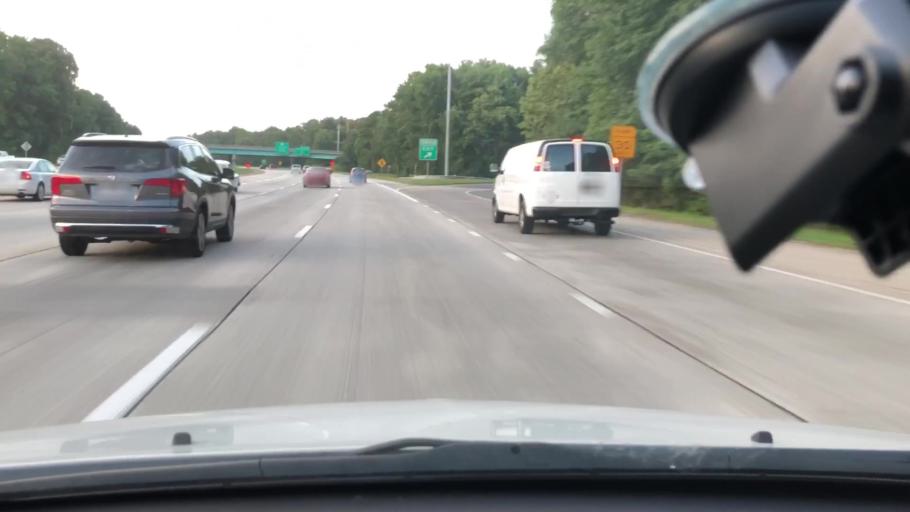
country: US
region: Virginia
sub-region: City of Chesapeake
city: Chesapeake
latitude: 36.8041
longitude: -76.1967
